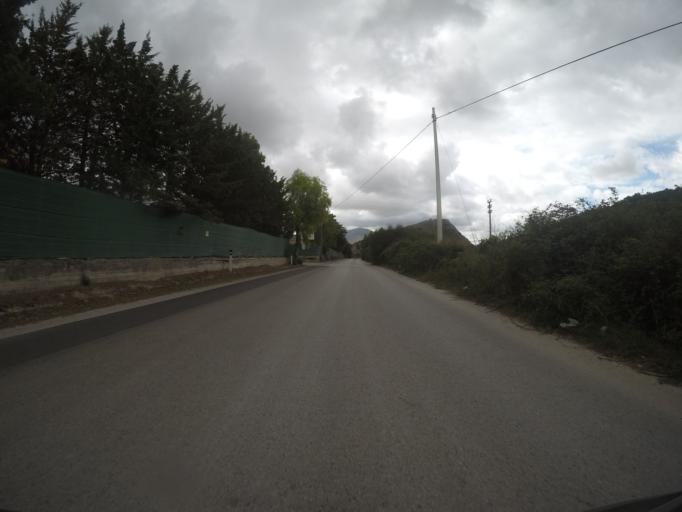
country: IT
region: Sicily
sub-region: Palermo
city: Montelepre
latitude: 38.1045
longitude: 13.1710
